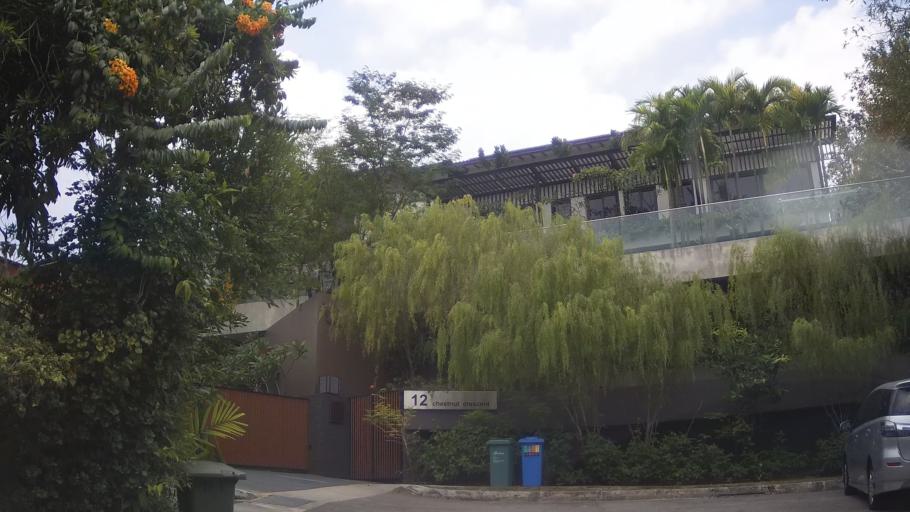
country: MY
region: Johor
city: Johor Bahru
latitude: 1.3717
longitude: 103.7708
